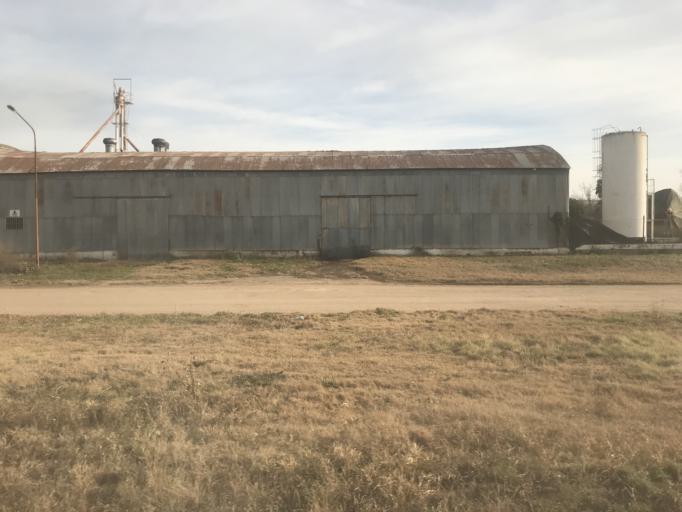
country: AR
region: Cordoba
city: Pilar
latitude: -31.6770
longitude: -63.8903
